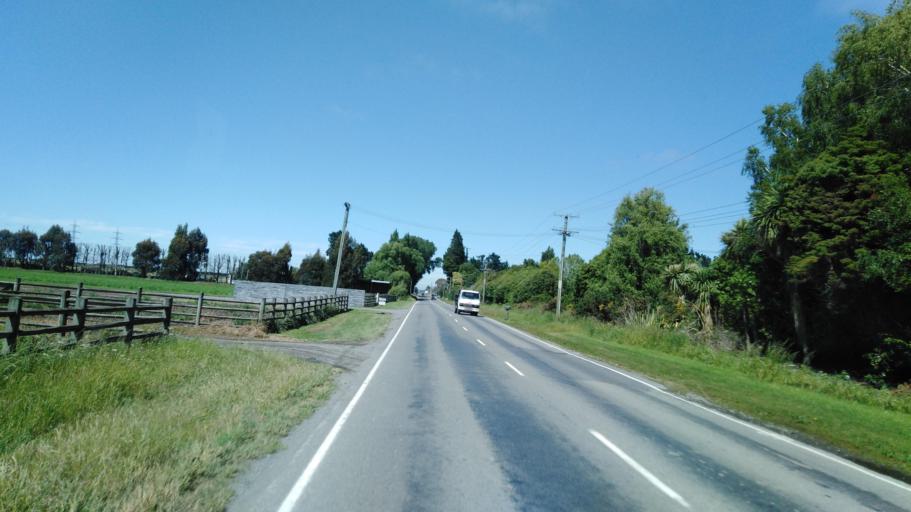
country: NZ
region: Canterbury
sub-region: Selwyn District
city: Prebbleton
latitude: -43.5220
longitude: 172.5034
